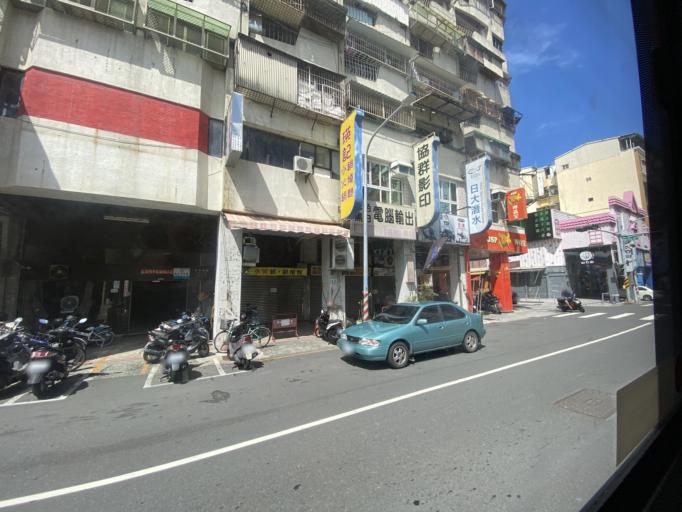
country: TW
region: Kaohsiung
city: Kaohsiung
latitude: 22.6236
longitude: 120.2708
